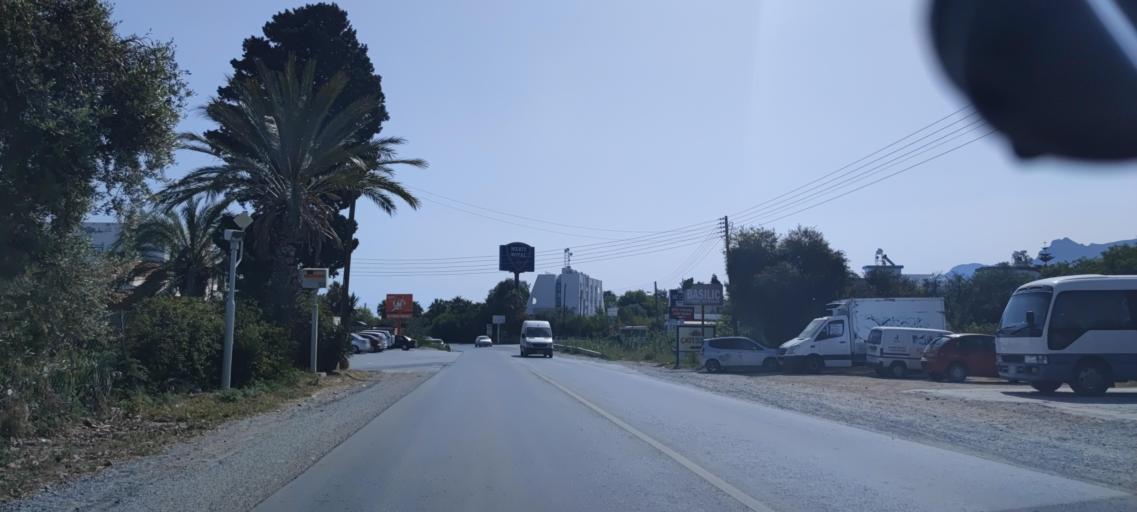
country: CY
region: Keryneia
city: Lapithos
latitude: 35.3475
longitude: 33.2103
